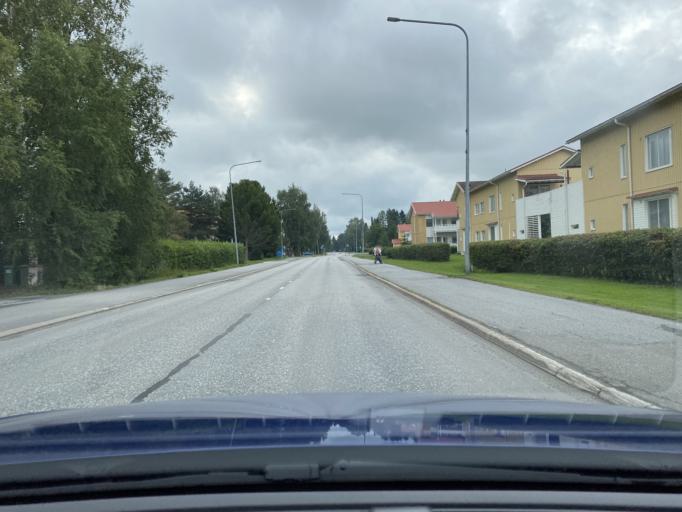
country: FI
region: Ostrobothnia
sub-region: Kyroenmaa
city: Laihia
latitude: 62.9749
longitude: 22.0152
